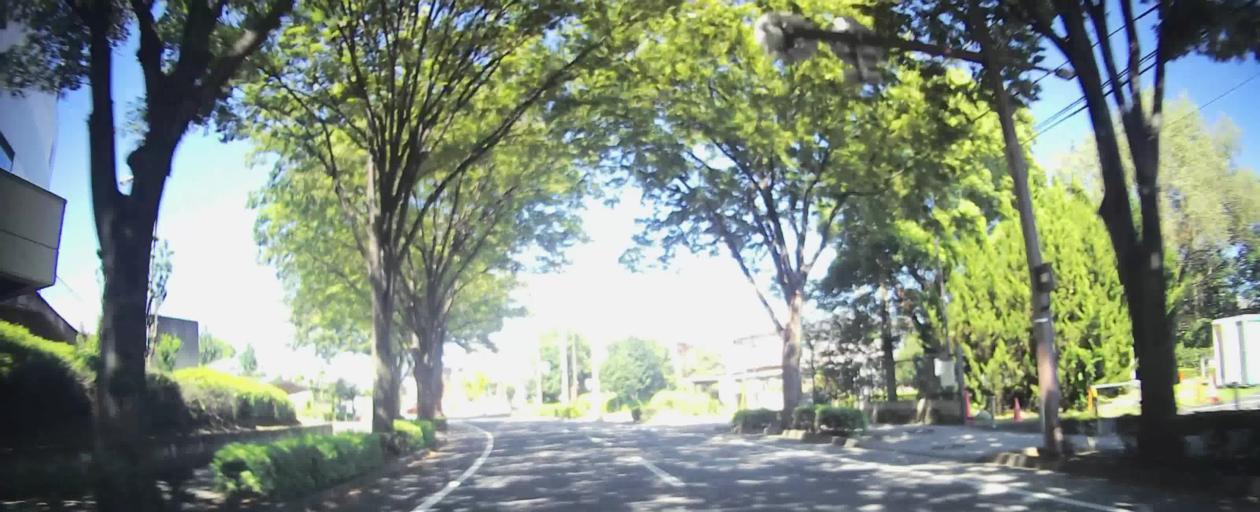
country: JP
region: Gunma
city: Maebashi-shi
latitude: 36.3979
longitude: 139.0587
